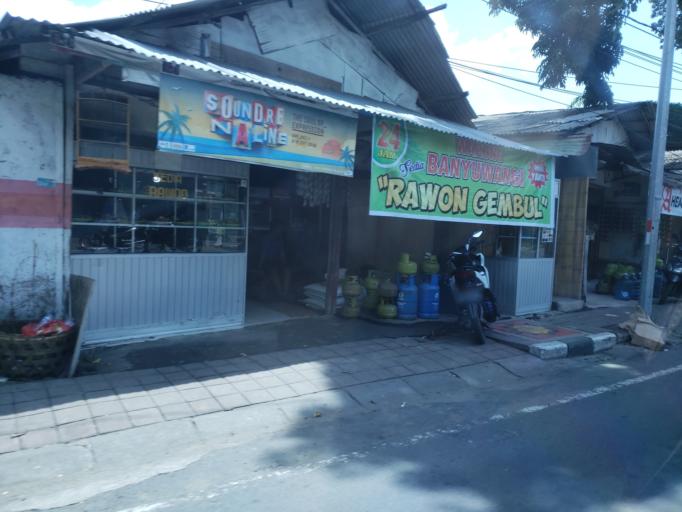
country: ID
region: Bali
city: Kelanabian
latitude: -8.7512
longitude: 115.1797
